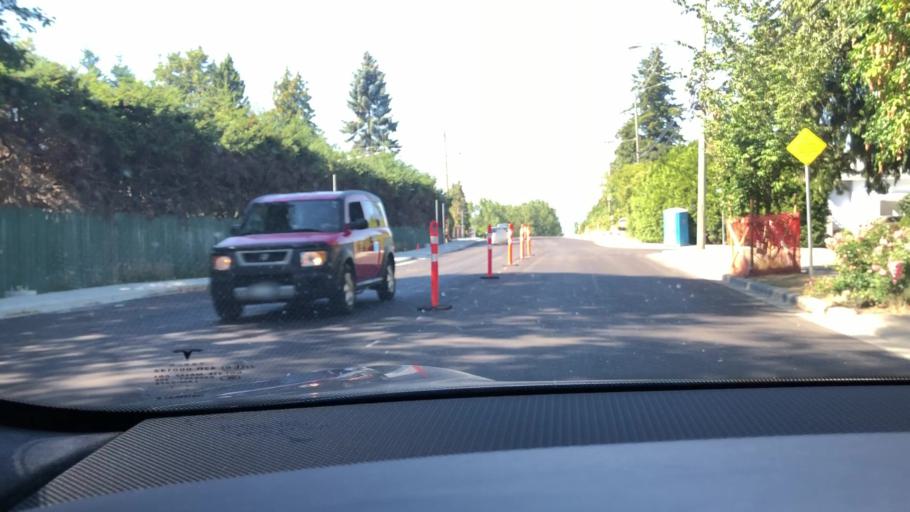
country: US
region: Washington
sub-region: Whatcom County
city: Point Roberts
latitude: 49.0277
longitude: -123.0797
